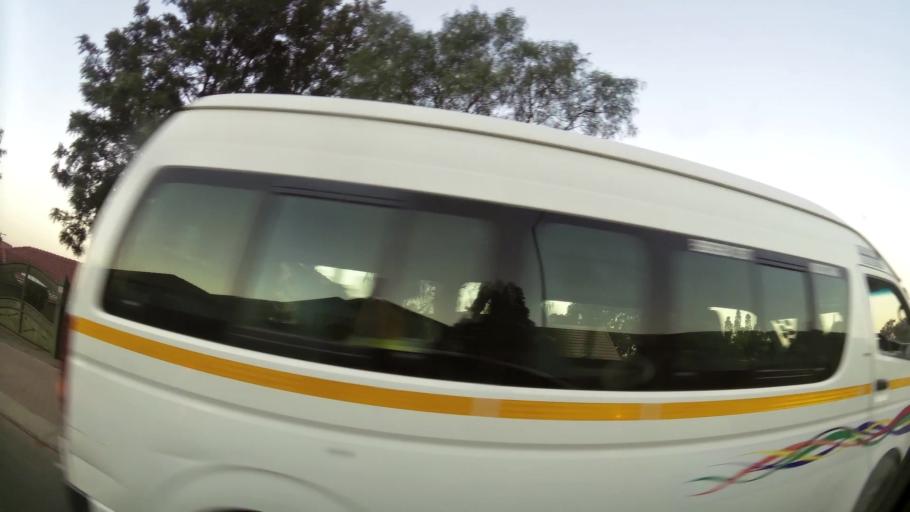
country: ZA
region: North-West
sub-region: Bojanala Platinum District Municipality
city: Rustenburg
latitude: -25.6555
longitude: 27.2027
